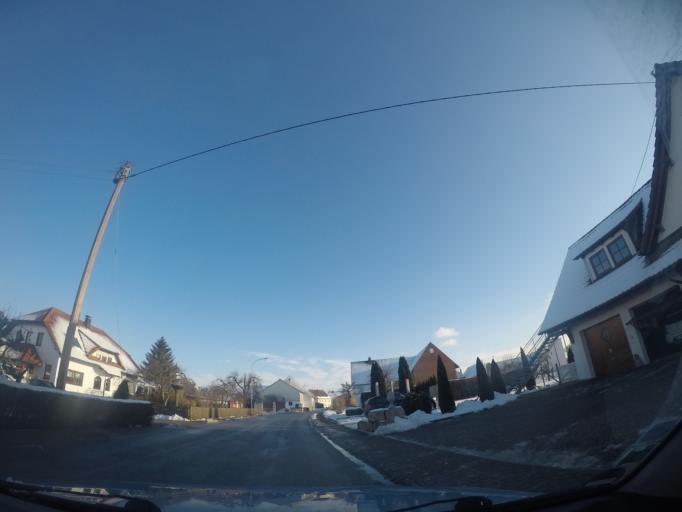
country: DE
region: Baden-Wuerttemberg
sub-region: Tuebingen Region
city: Dettingen
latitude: 48.2326
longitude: 9.7301
